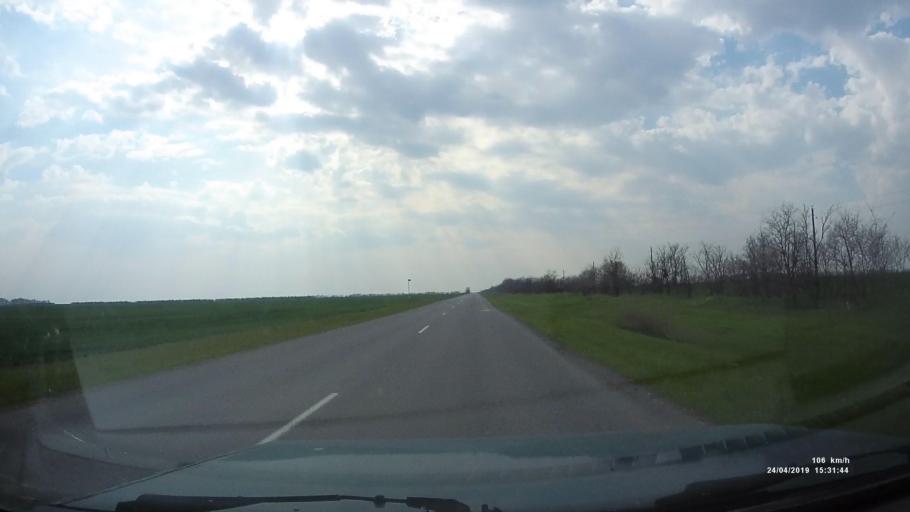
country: RU
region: Rostov
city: Remontnoye
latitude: 46.5997
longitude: 42.9768
